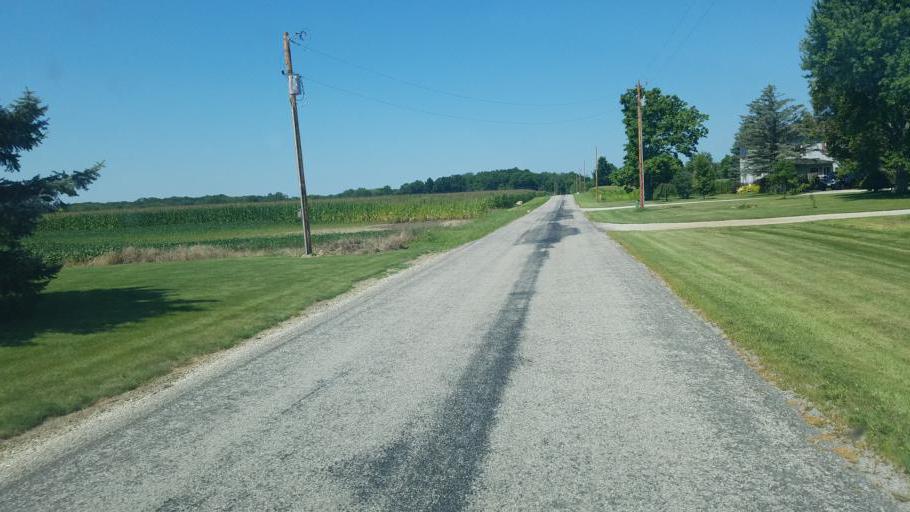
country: US
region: Ohio
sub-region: Delaware County
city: Ashley
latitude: 40.4342
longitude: -83.0322
